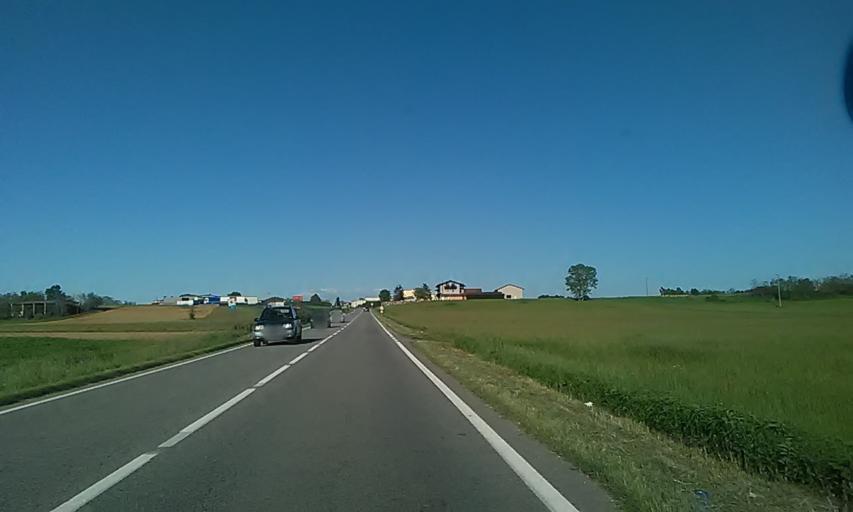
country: IT
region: Piedmont
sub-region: Provincia di Novara
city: Mezzomerico
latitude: 45.5877
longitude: 8.5884
